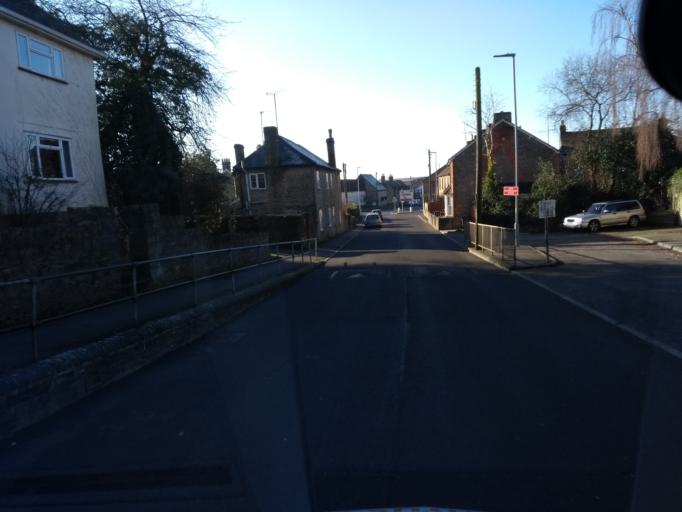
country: GB
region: England
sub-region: Somerset
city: Wincanton
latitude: 51.0534
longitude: -2.4111
